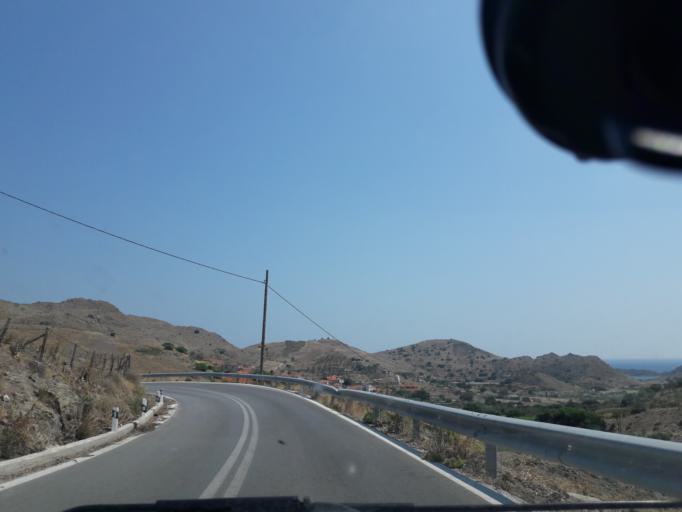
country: GR
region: North Aegean
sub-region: Nomos Lesvou
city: Myrina
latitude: 39.8596
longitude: 25.0816
